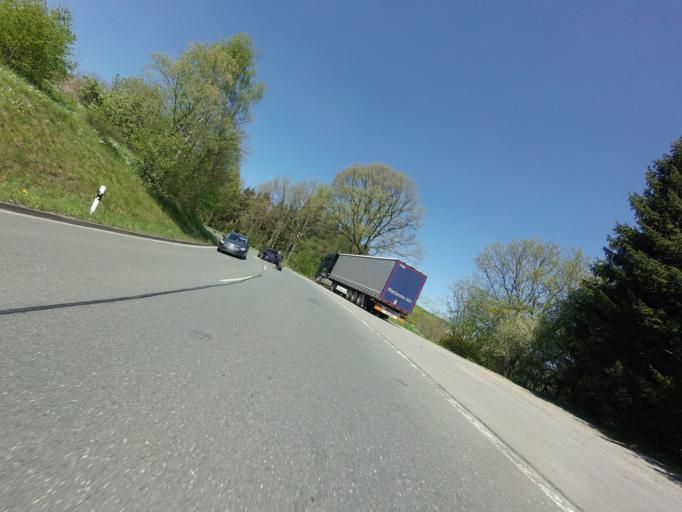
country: DE
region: North Rhine-Westphalia
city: Kreuztal
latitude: 50.9997
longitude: 7.9535
